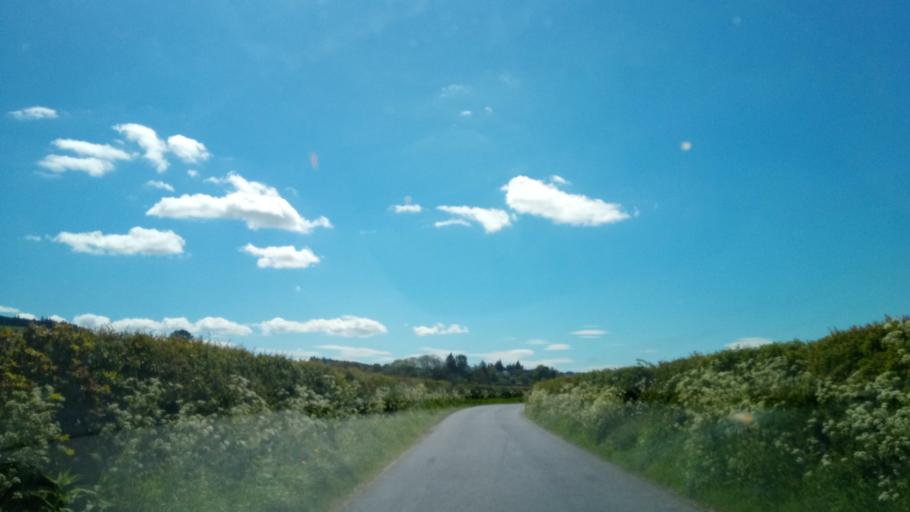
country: GB
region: Scotland
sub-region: The Scottish Borders
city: Saint Boswells
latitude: 55.4653
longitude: -2.6804
